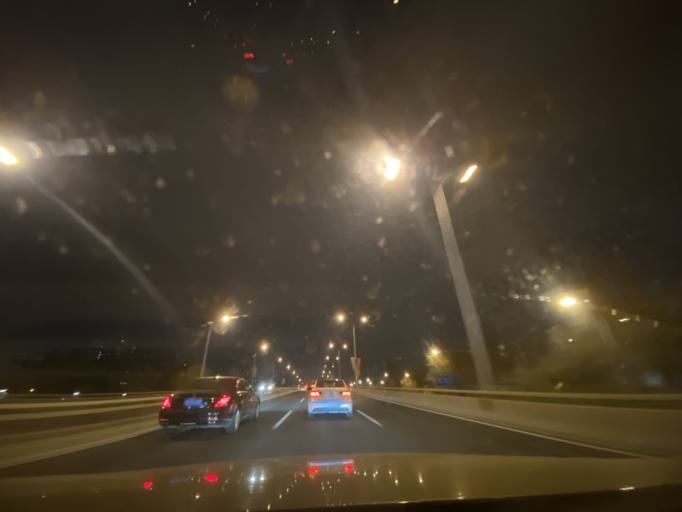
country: CN
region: Beijing
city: Lugouqiao
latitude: 39.8959
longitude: 116.2797
